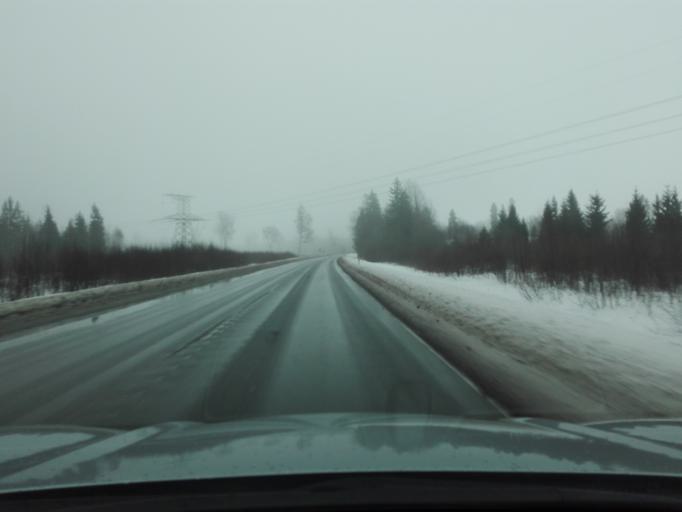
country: EE
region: Raplamaa
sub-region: Kohila vald
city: Kohila
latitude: 59.2346
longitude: 24.7685
